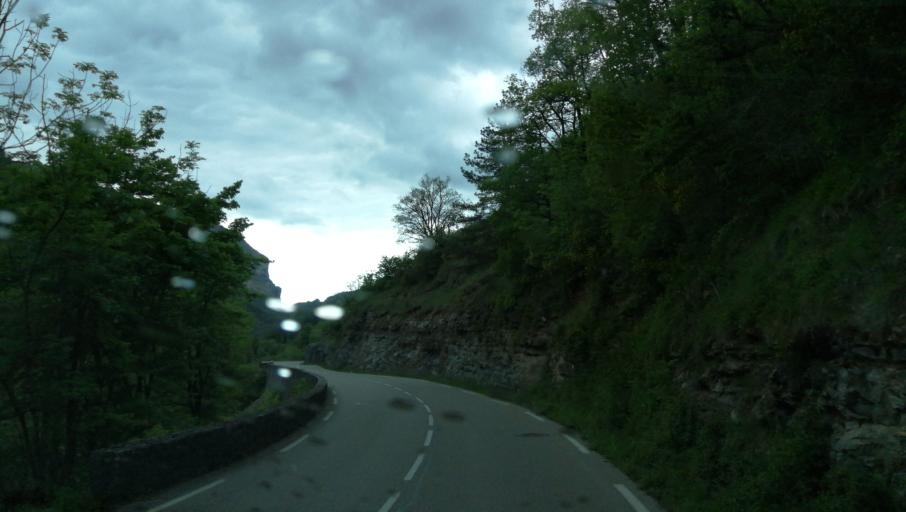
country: FR
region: Rhone-Alpes
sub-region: Departement de l'Isere
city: Pont-en-Royans
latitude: 45.0680
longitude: 5.3850
